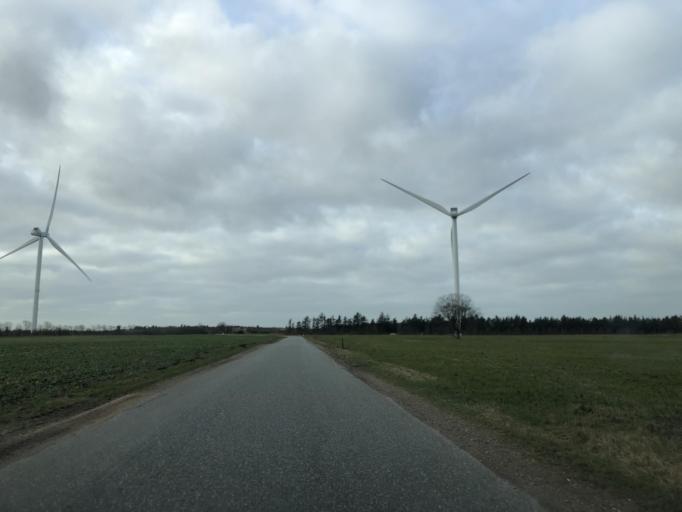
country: DK
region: Central Jutland
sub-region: Lemvig Kommune
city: Lemvig
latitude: 56.4397
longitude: 8.3486
